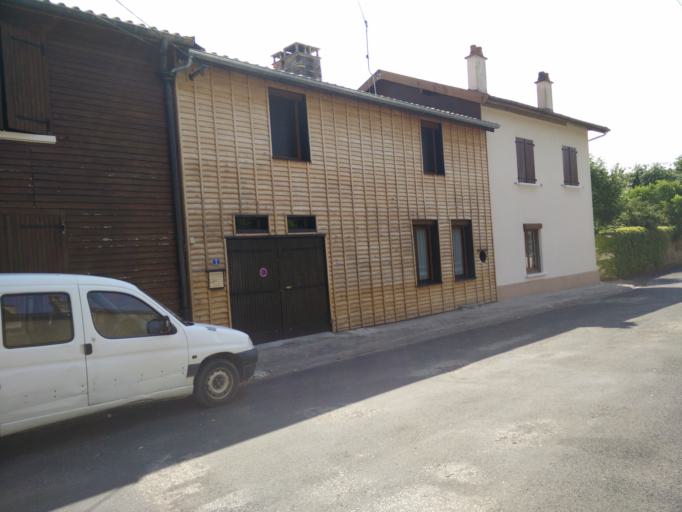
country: FR
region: Champagne-Ardenne
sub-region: Departement de la Haute-Marne
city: Villiers-en-Lieu
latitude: 48.5891
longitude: 4.8655
